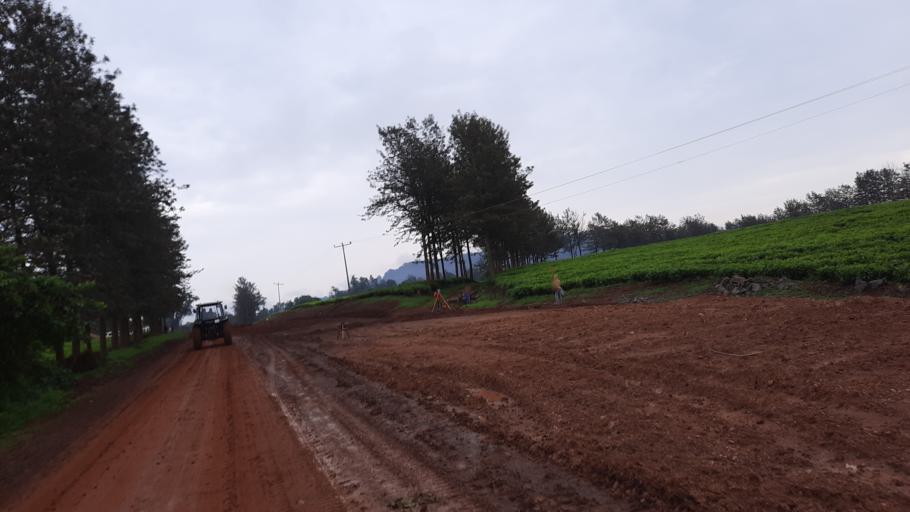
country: ET
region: Oromiya
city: Gore
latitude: 7.8593
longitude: 35.4765
